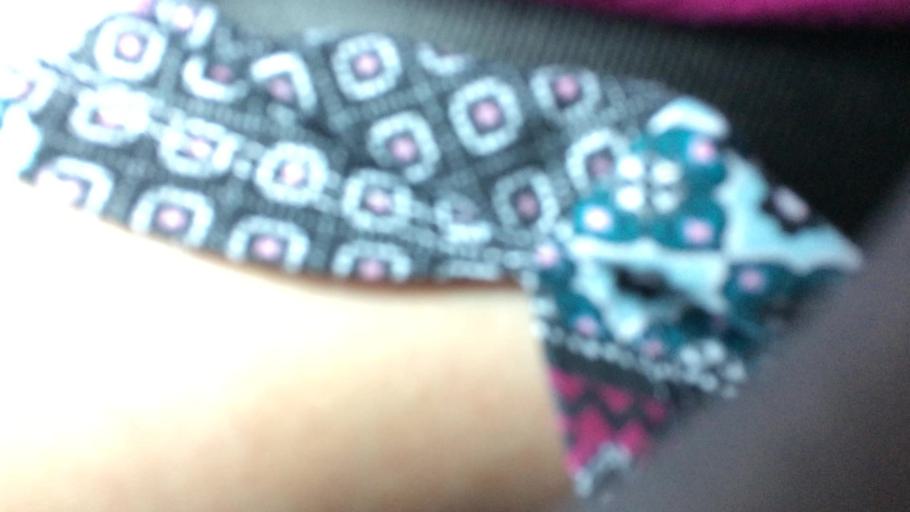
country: US
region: New Mexico
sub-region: Colfax County
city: Springer
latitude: 36.0656
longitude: -104.6910
